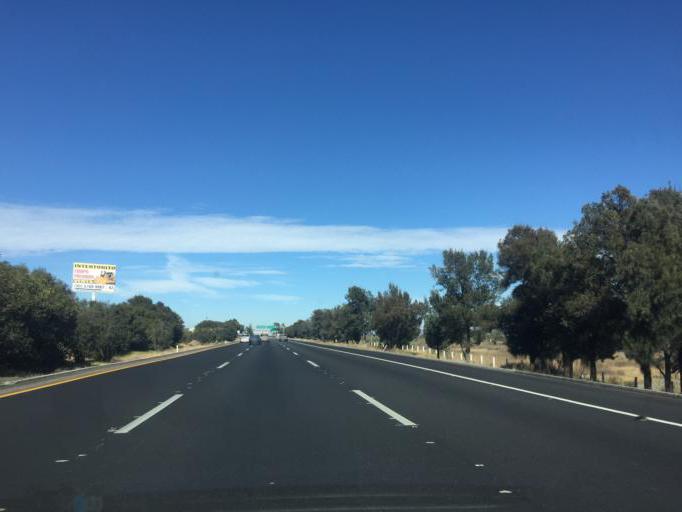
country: MX
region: Hidalgo
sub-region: Huichapan
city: Llano Largo
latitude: 20.2204
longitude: -99.8038
